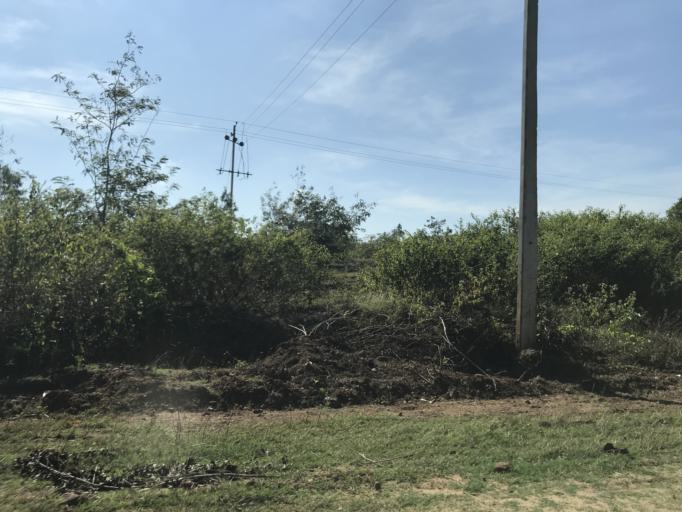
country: IN
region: Karnataka
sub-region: Mysore
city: Heggadadevankote
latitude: 12.0422
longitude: 76.3316
